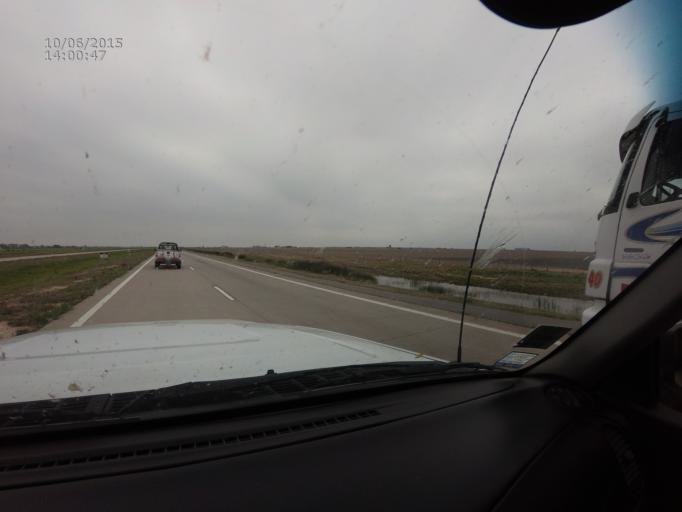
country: AR
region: Cordoba
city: Morrison
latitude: -32.5388
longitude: -62.8978
